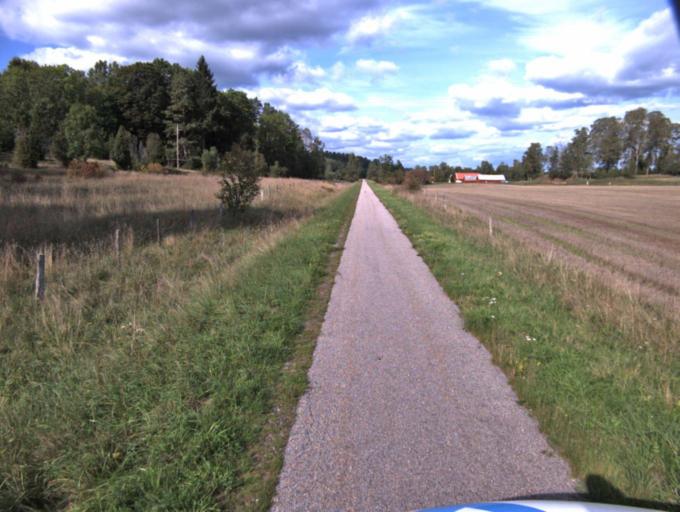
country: SE
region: Vaestra Goetaland
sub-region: Ulricehamns Kommun
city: Ulricehamn
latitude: 57.8811
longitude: 13.4307
